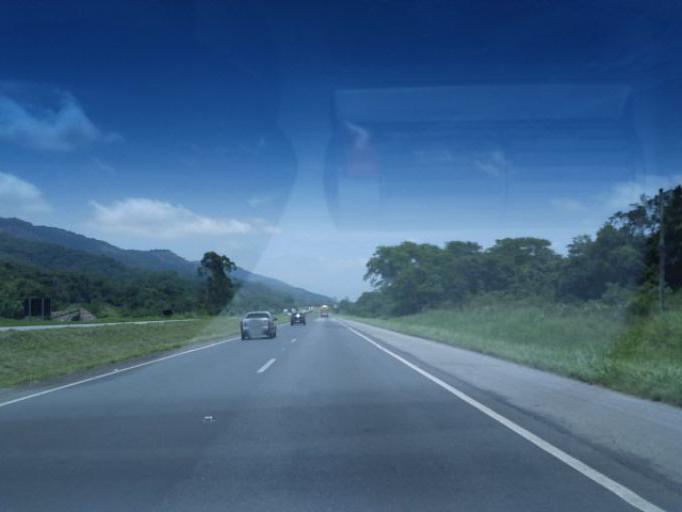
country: BR
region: Sao Paulo
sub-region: Miracatu
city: Miracatu
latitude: -24.2739
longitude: -47.4094
